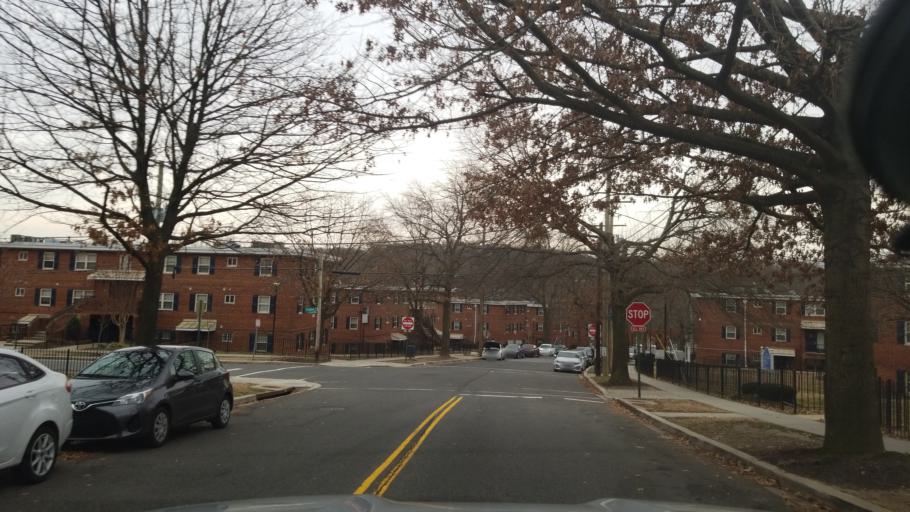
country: US
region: Maryland
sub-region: Prince George's County
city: Hillcrest Heights
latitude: 38.8450
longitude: -76.9791
